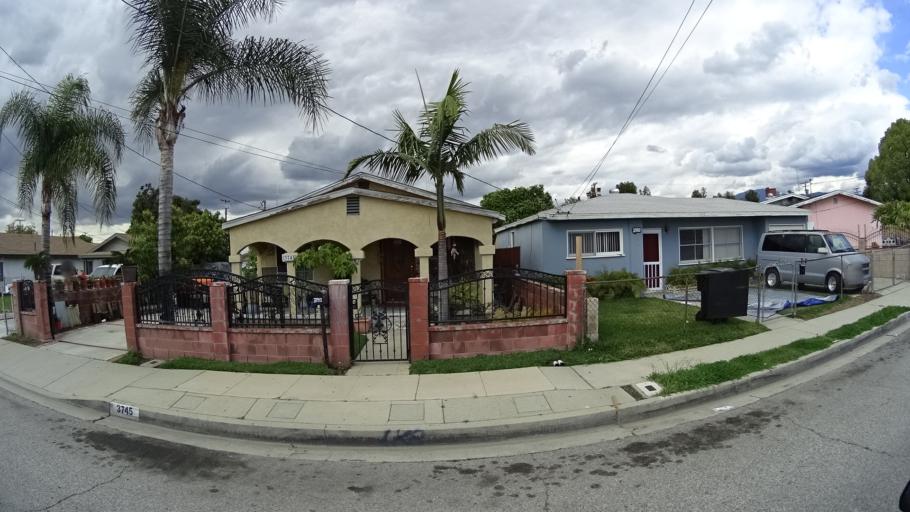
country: US
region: California
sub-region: Los Angeles County
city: Baldwin Park
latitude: 34.0830
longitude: -117.9599
